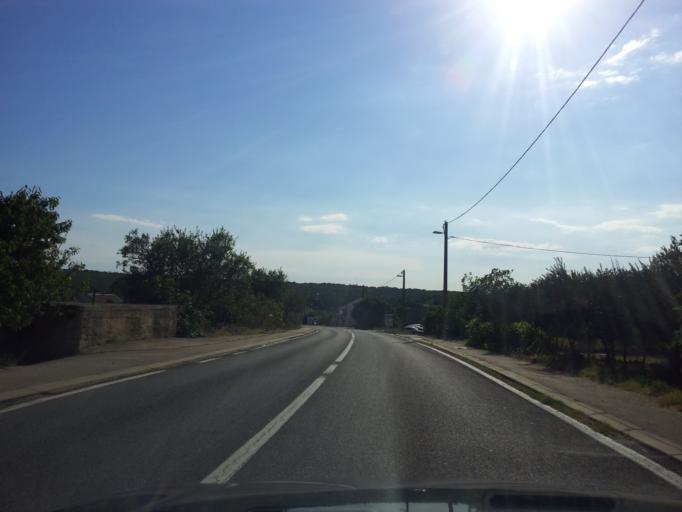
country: HR
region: Zadarska
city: Posedarje
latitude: 44.2137
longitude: 15.4751
